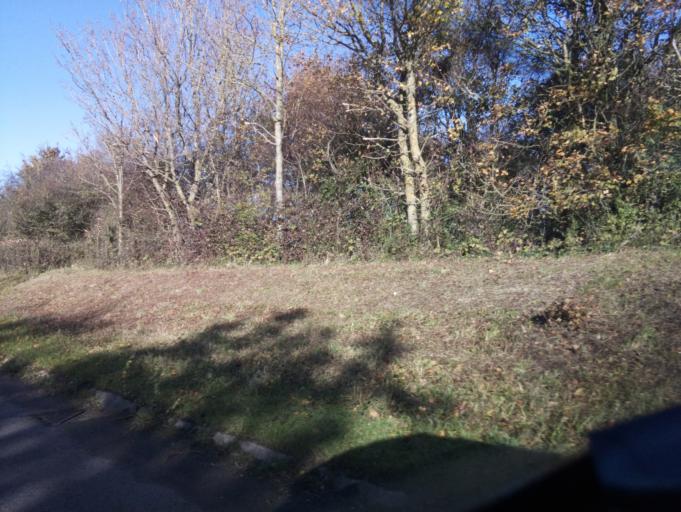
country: GB
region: England
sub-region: Somerset
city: Stoke-sub-Hamdon
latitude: 50.9737
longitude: -2.7245
